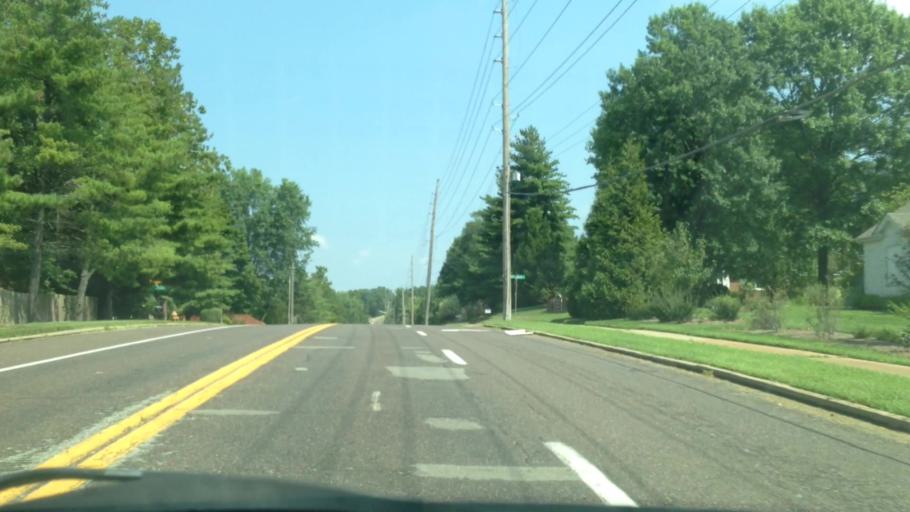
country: US
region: Missouri
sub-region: Saint Louis County
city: Des Peres
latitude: 38.5930
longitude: -90.4441
